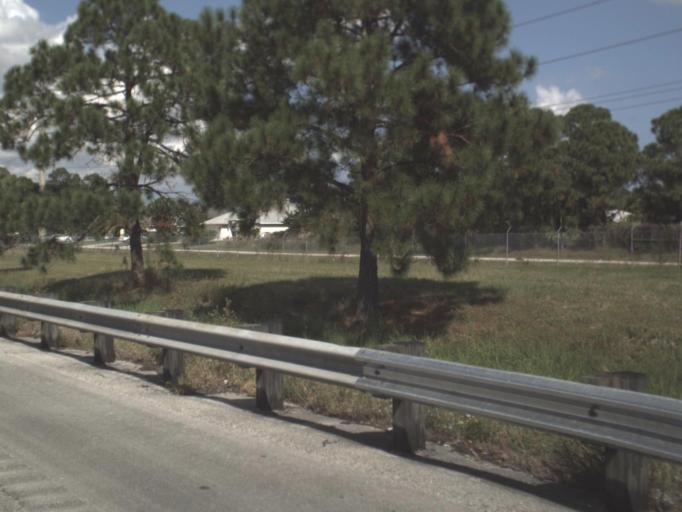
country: US
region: Florida
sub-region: Saint Lucie County
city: Port Saint Lucie
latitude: 27.2685
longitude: -80.3556
